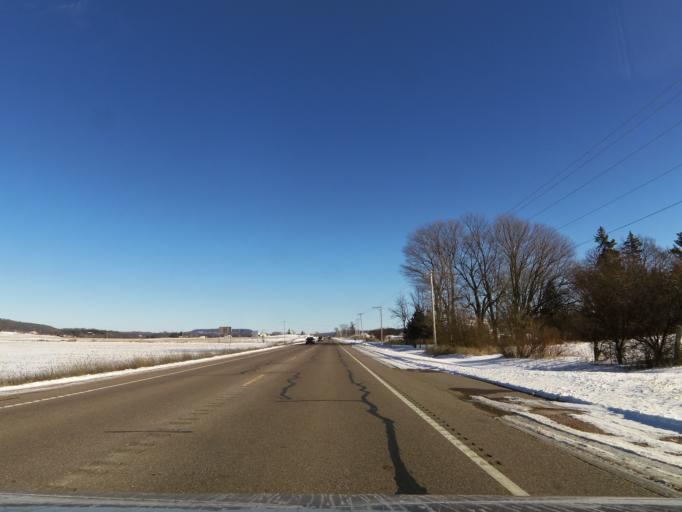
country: US
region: Wisconsin
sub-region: Sauk County
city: Baraboo
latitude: 43.4743
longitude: -89.6830
